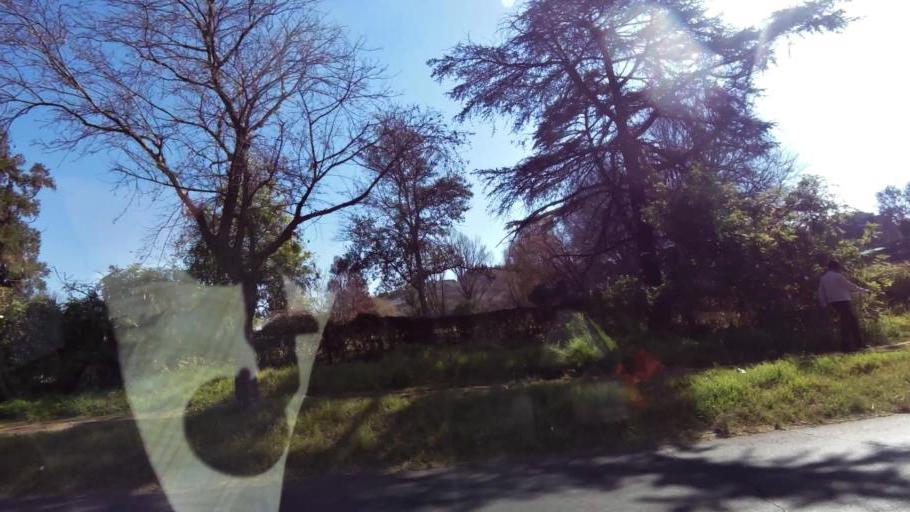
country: ZA
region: Gauteng
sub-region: City of Johannesburg Metropolitan Municipality
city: Johannesburg
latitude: -26.1511
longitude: 27.9822
